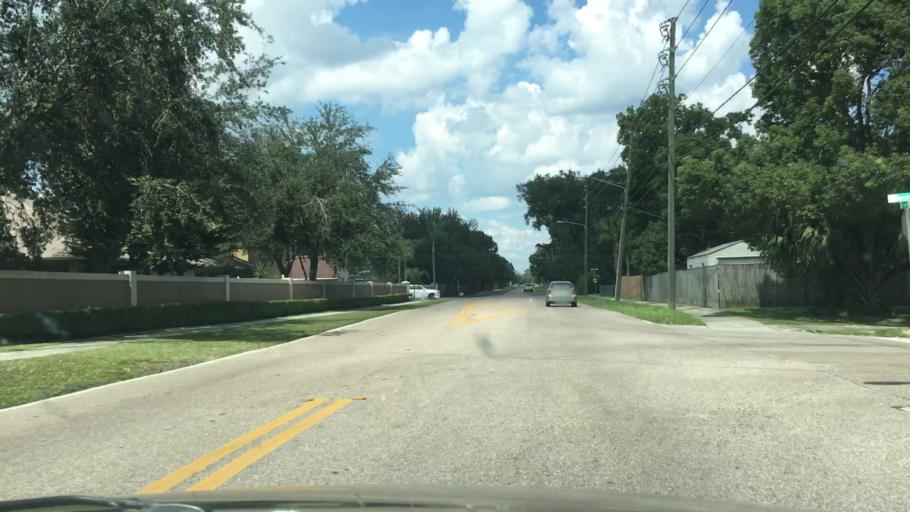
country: US
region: Florida
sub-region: Orange County
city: Lockhart
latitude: 28.6326
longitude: -81.4436
